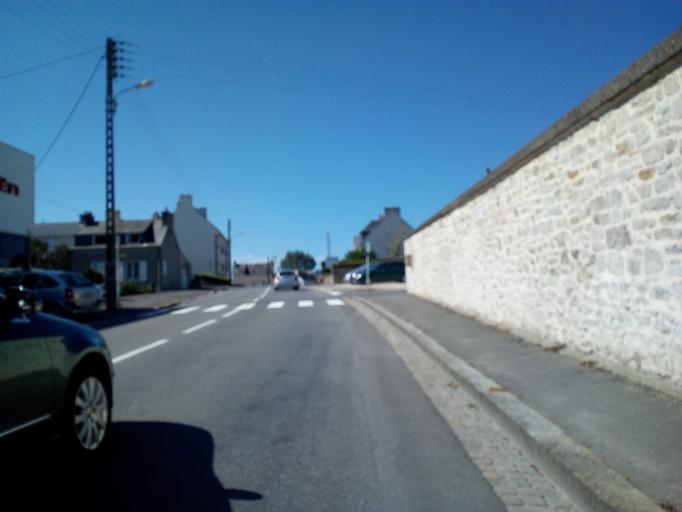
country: FR
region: Brittany
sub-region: Departement du Finistere
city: Landivisiau
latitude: 48.5135
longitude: -4.0713
